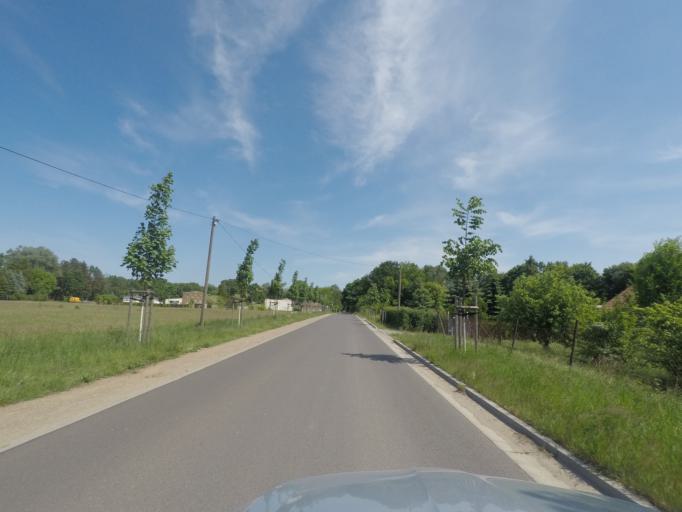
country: DE
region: Brandenburg
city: Melchow
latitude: 52.8507
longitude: 13.7057
